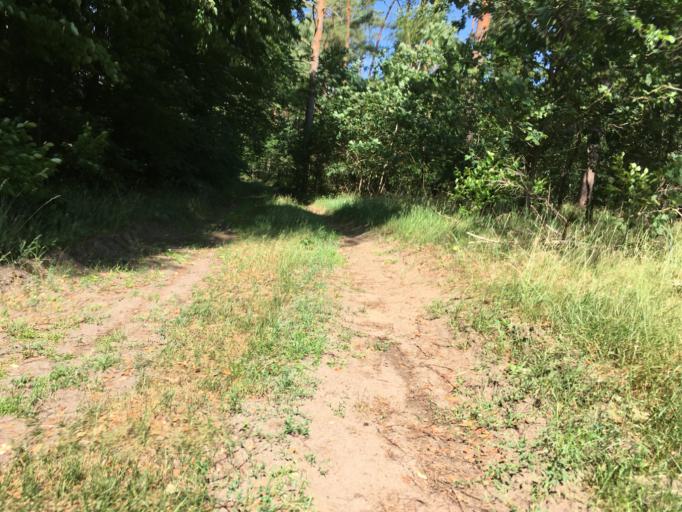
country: DE
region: Brandenburg
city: Marienwerder
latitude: 52.9215
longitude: 13.6592
